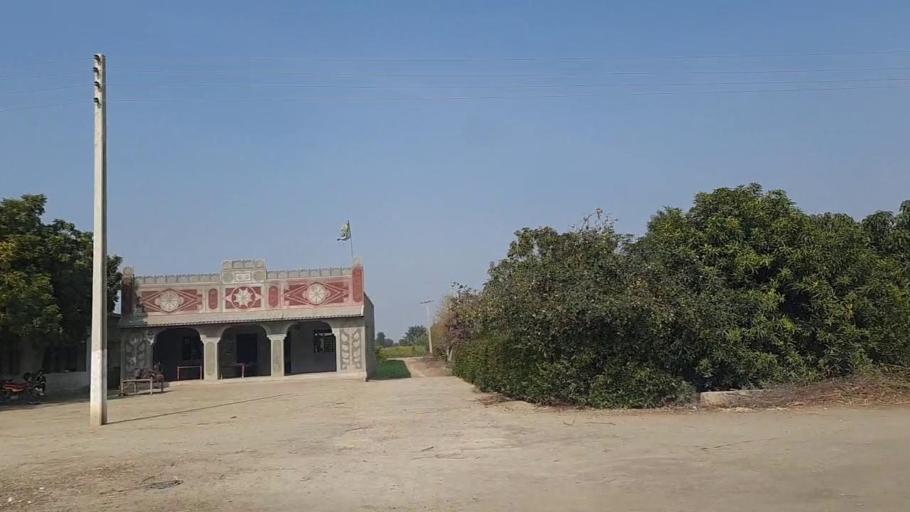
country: PK
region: Sindh
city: Daur
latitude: 26.4940
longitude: 68.4489
